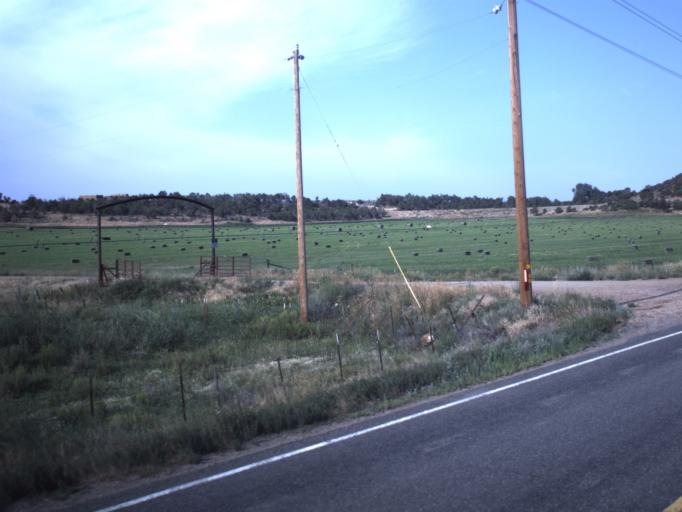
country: US
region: Utah
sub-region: Duchesne County
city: Duchesne
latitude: 40.3556
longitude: -110.3553
